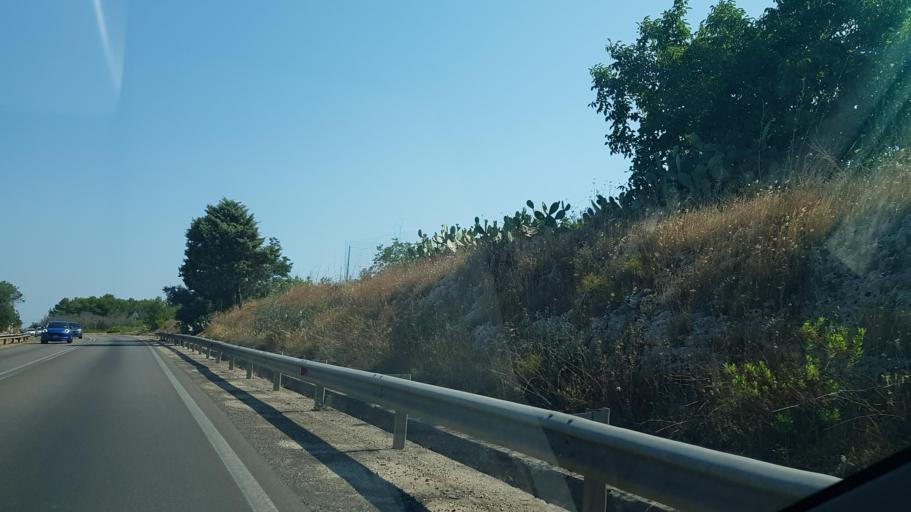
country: IT
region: Apulia
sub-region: Provincia di Lecce
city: Nociglia
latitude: 40.0427
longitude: 18.3222
